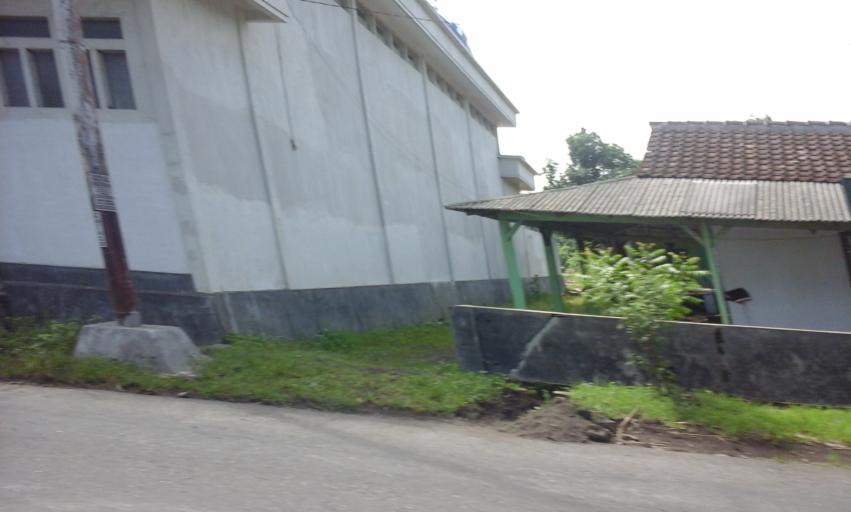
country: ID
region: East Java
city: Sumberpinang Satu
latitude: -8.1735
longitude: 113.8116
